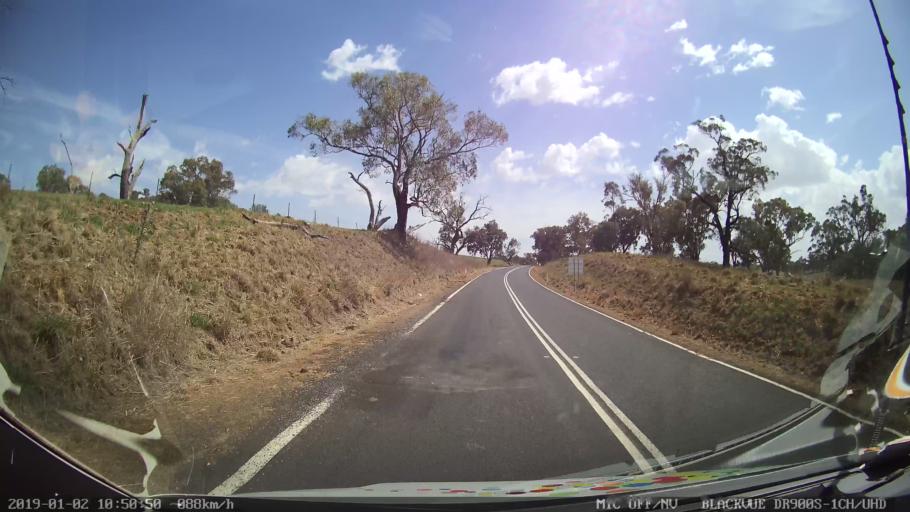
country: AU
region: New South Wales
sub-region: Cootamundra
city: Cootamundra
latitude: -34.7085
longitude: 148.2755
